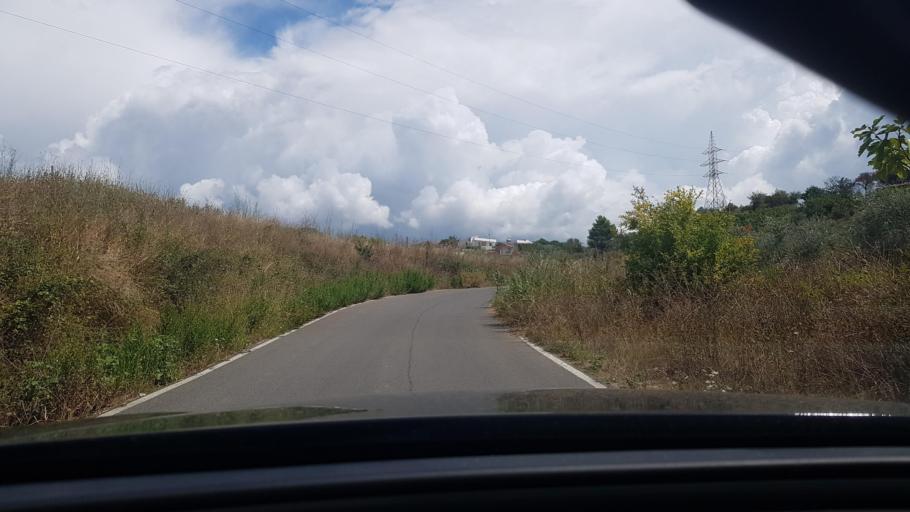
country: AL
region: Durres
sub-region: Rrethi i Durresit
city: Rrashbull
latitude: 41.2973
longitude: 19.5258
